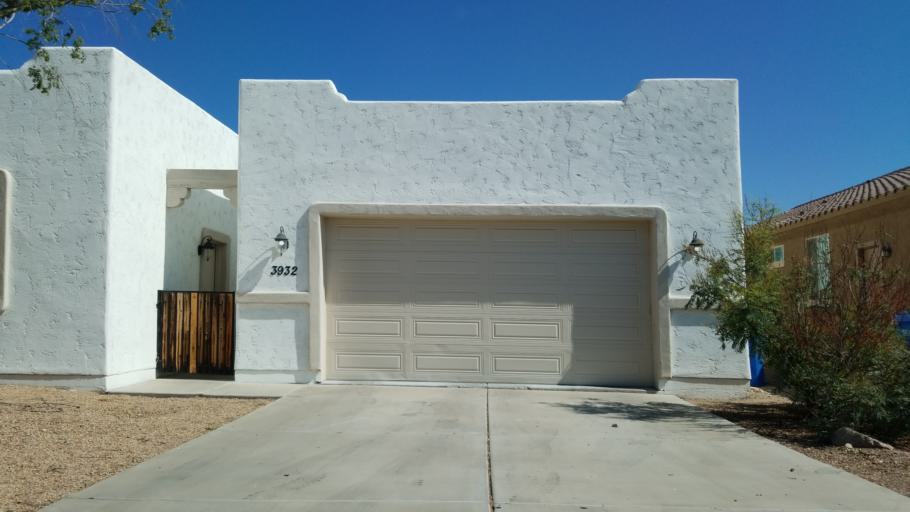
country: US
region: Arizona
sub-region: Maricopa County
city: Peoria
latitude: 33.6798
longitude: -112.1447
